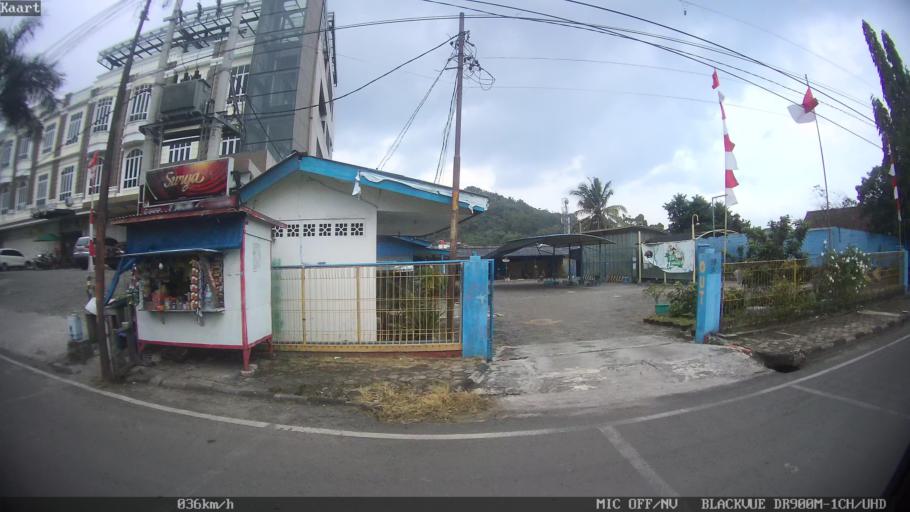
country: ID
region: Lampung
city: Bandarlampung
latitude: -5.4316
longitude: 105.2757
